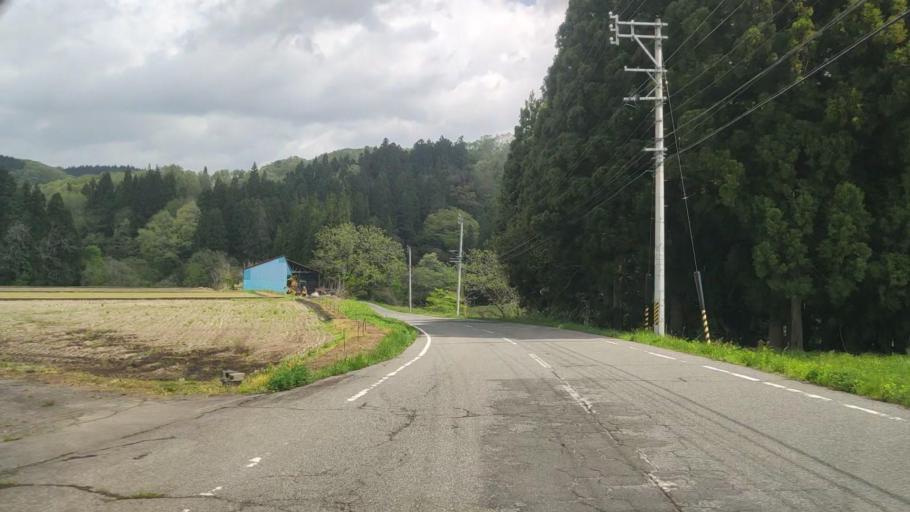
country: JP
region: Fukushima
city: Kitakata
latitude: 37.6566
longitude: 139.5901
